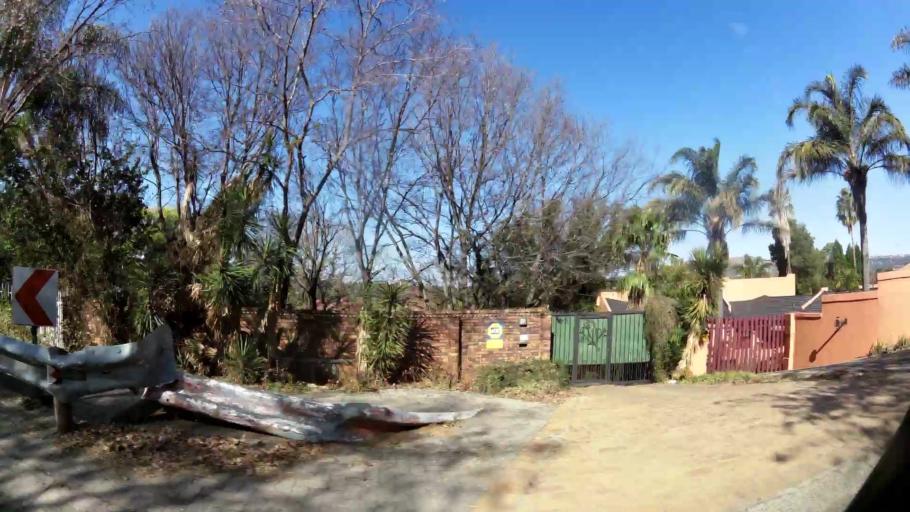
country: ZA
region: Gauteng
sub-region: City of Johannesburg Metropolitan Municipality
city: Roodepoort
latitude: -26.1115
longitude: 27.9606
